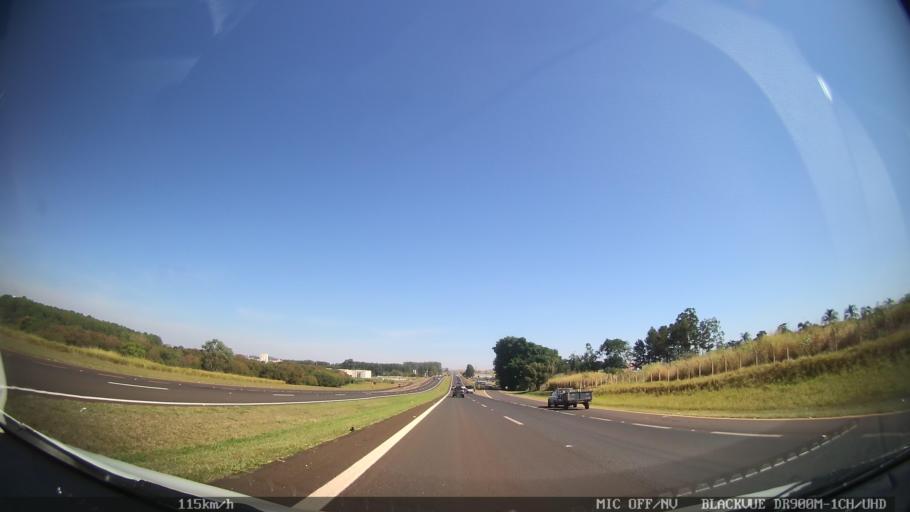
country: BR
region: Sao Paulo
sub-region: Ribeirao Preto
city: Ribeirao Preto
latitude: -21.1147
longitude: -47.8238
